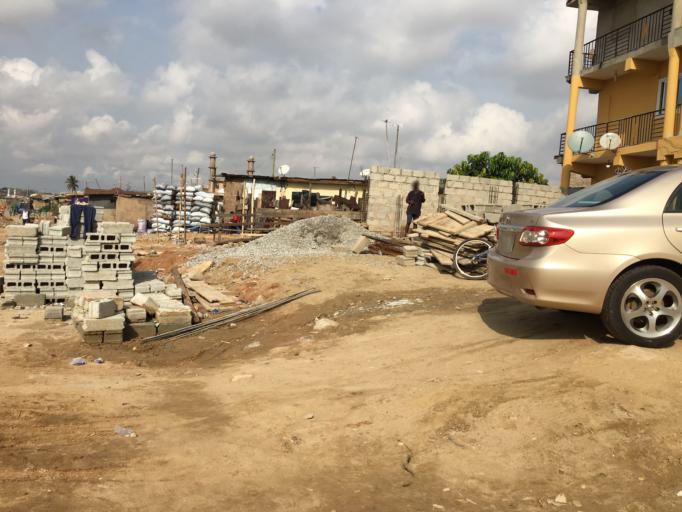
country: GH
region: Greater Accra
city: Accra
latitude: 5.5922
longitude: -0.1901
